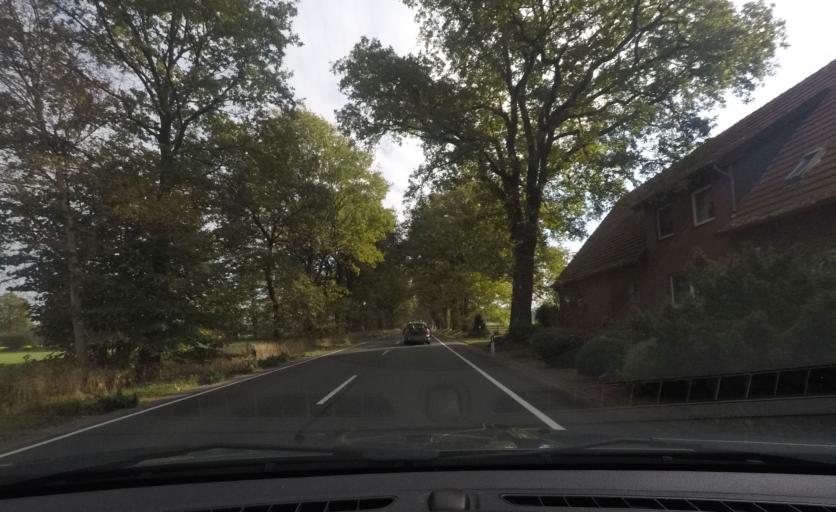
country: DE
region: North Rhine-Westphalia
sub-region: Regierungsbezirk Munster
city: Dulmen
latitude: 51.8480
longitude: 7.1866
